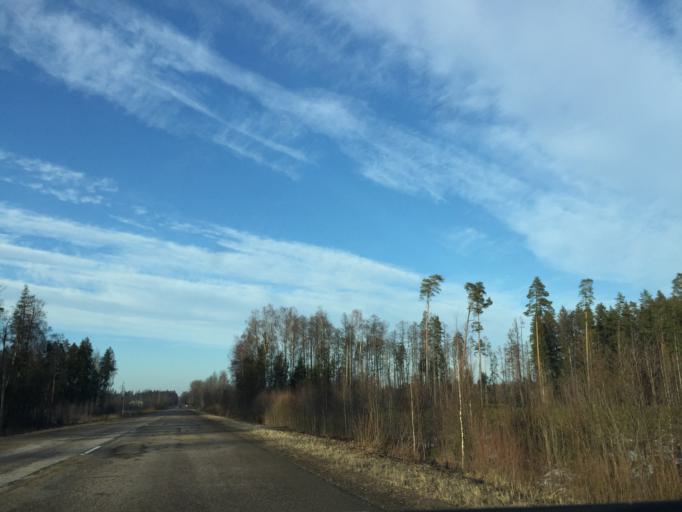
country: LV
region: Kekava
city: Balozi
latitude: 56.7276
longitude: 24.1103
